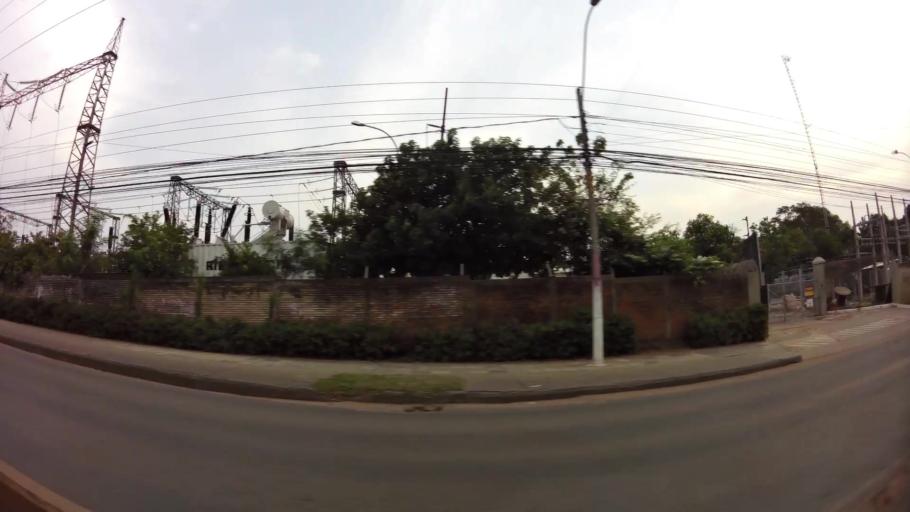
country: PY
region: Central
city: Lambare
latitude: -25.3433
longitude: -57.6199
